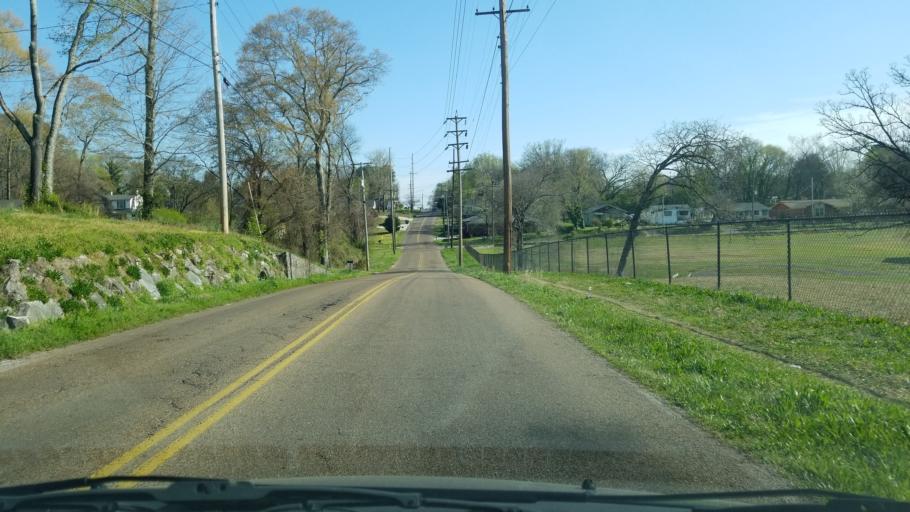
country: US
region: Tennessee
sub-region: Hamilton County
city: East Ridge
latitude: 35.0290
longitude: -85.2438
